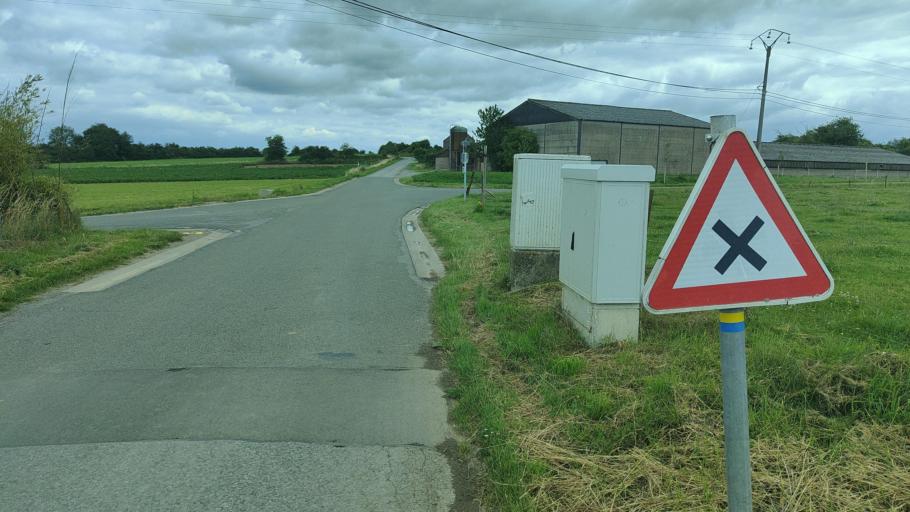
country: BE
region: Wallonia
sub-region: Province du Hainaut
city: Chimay
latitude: 50.0549
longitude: 4.3485
